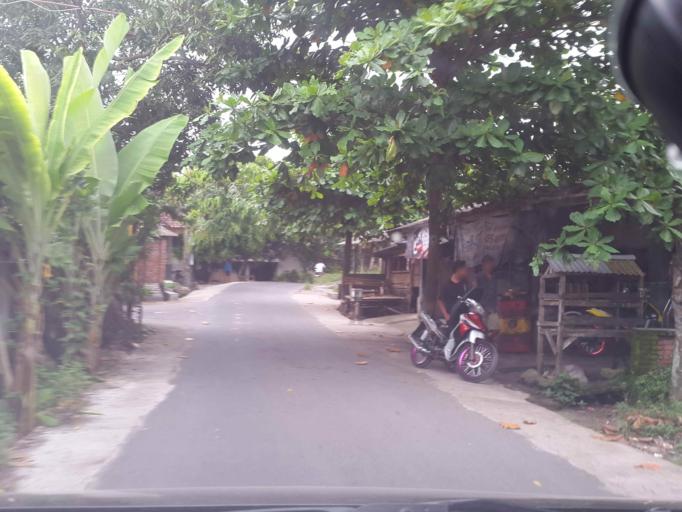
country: ID
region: West Nusa Tenggara
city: Mambalan
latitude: -8.5332
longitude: 116.0835
